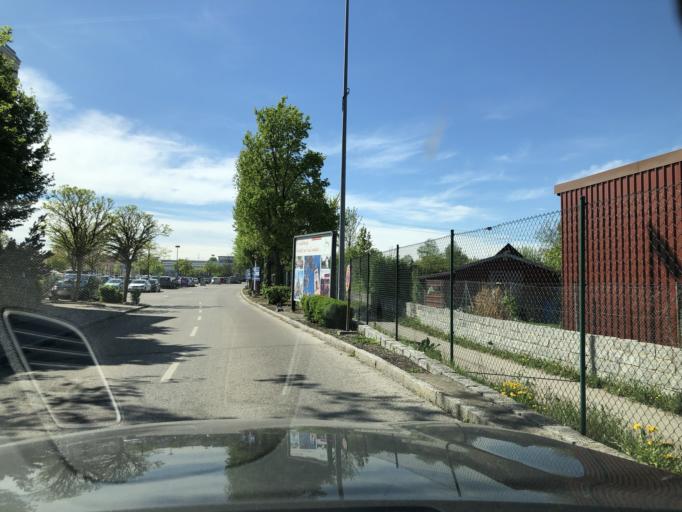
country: DE
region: Bavaria
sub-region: Swabia
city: Friedberg
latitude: 48.3558
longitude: 10.9694
